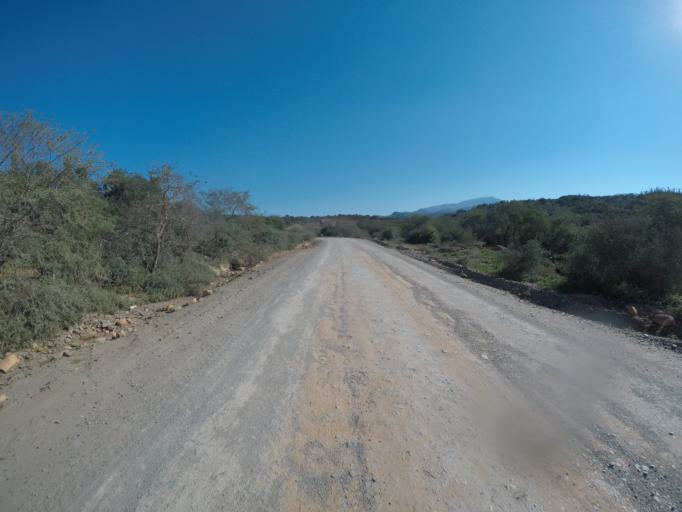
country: ZA
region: Eastern Cape
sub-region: Cacadu District Municipality
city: Kruisfontein
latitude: -33.6748
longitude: 24.5778
